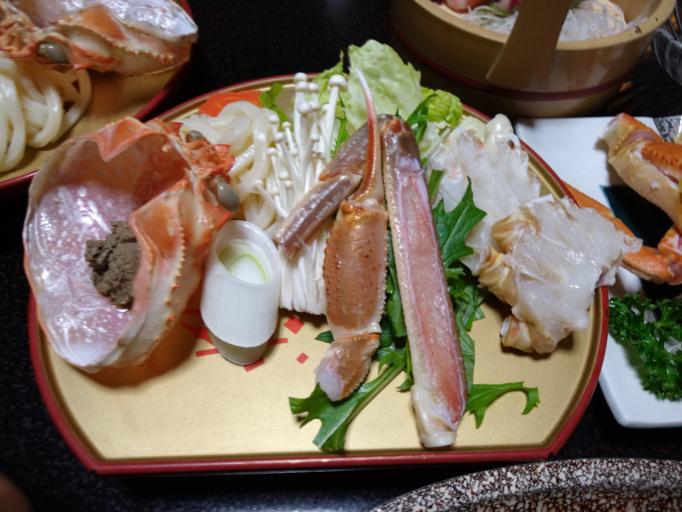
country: JP
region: Hyogo
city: Toyooka
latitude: 35.6270
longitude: 134.8145
